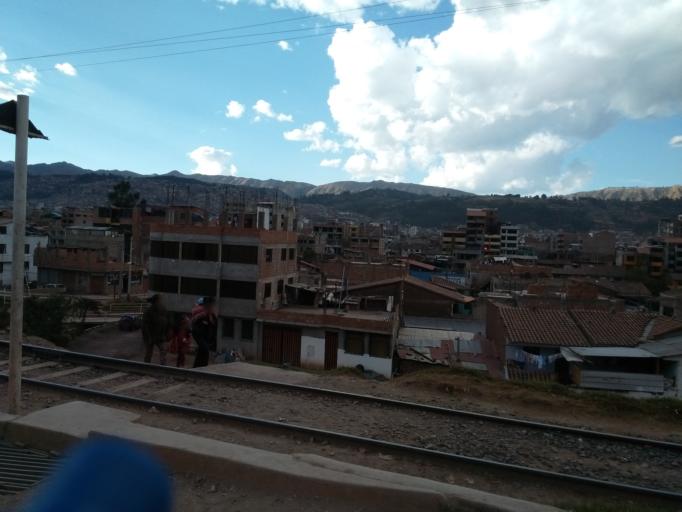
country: PE
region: Cusco
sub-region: Provincia de Cusco
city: Cusco
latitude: -13.5399
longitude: -71.9490
